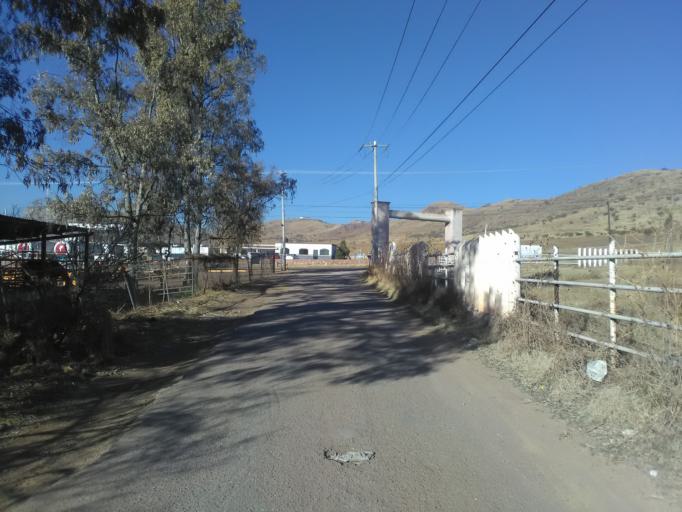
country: MX
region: Durango
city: Victoria de Durango
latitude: 24.0623
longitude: -104.6549
